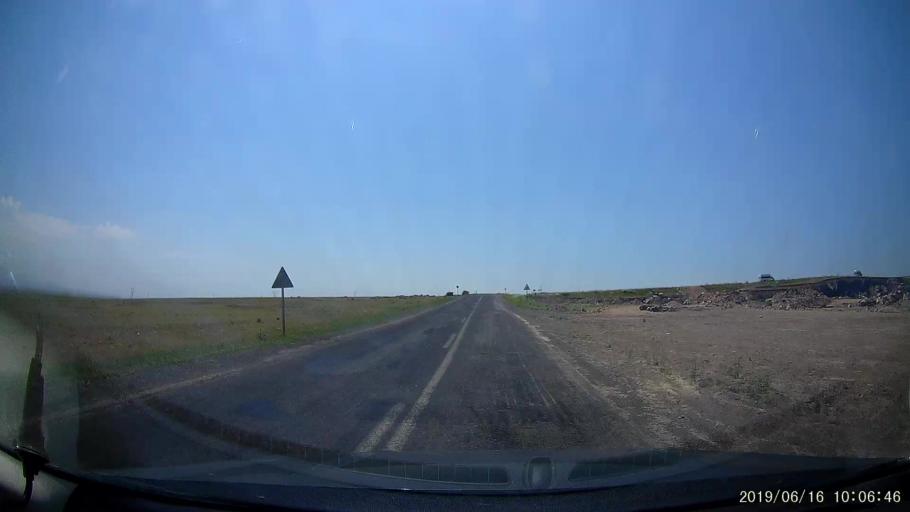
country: TR
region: Kars
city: Digor
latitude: 40.2514
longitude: 43.5464
